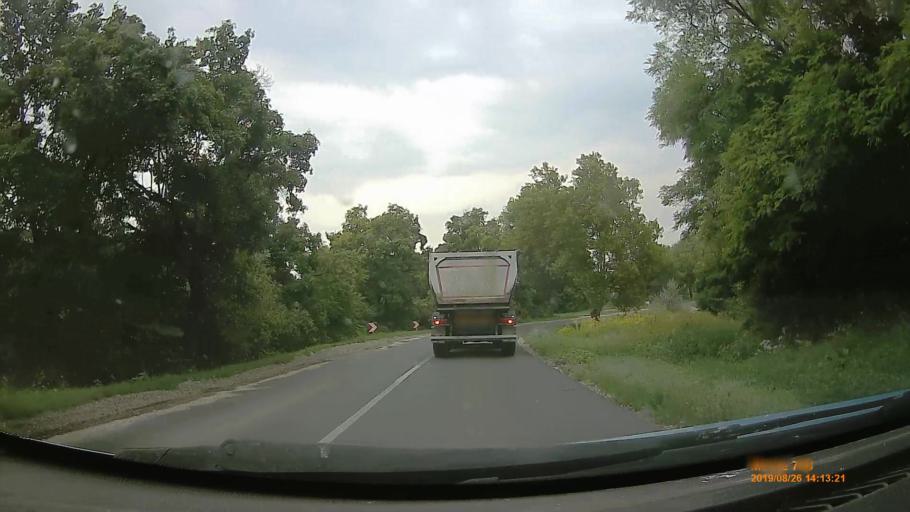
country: HU
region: Fejer
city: Csakvar
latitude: 47.4327
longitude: 18.5321
